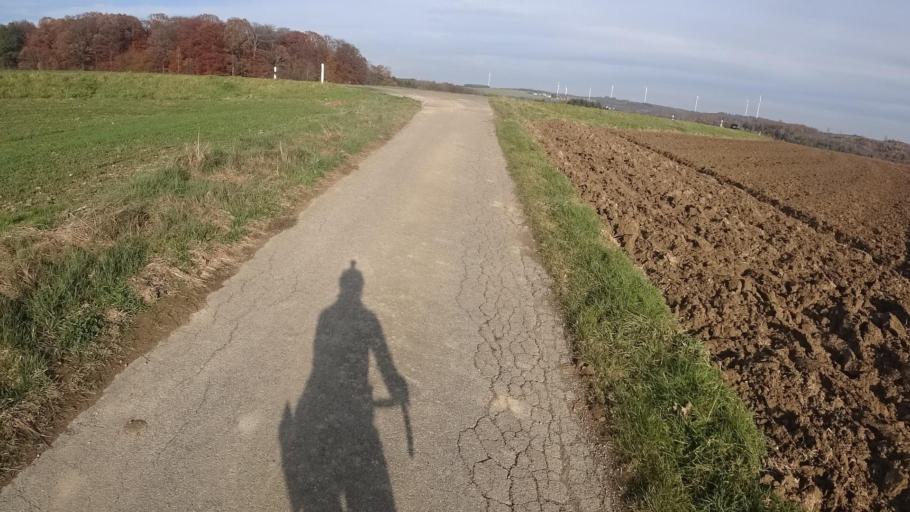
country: DE
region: Rheinland-Pfalz
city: Hausbay
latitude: 50.1081
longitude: 7.5499
